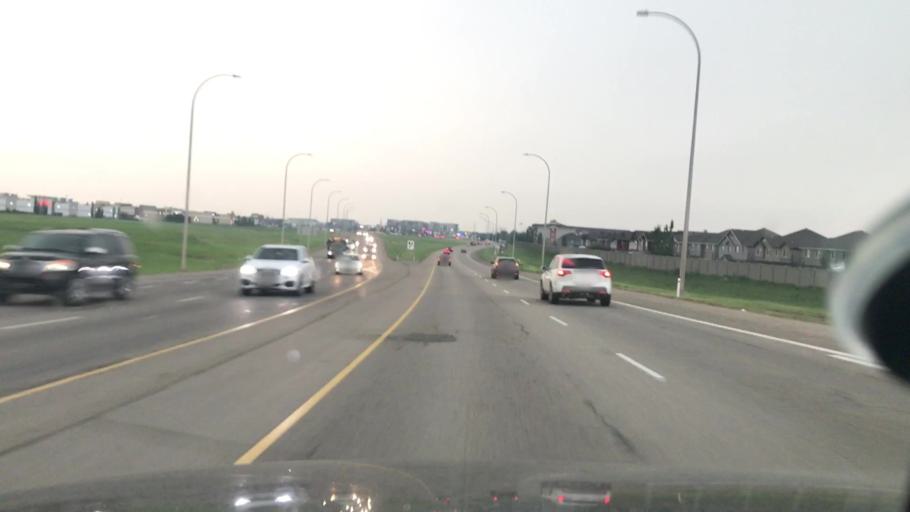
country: CA
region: Alberta
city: Devon
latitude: 53.4429
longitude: -113.6042
